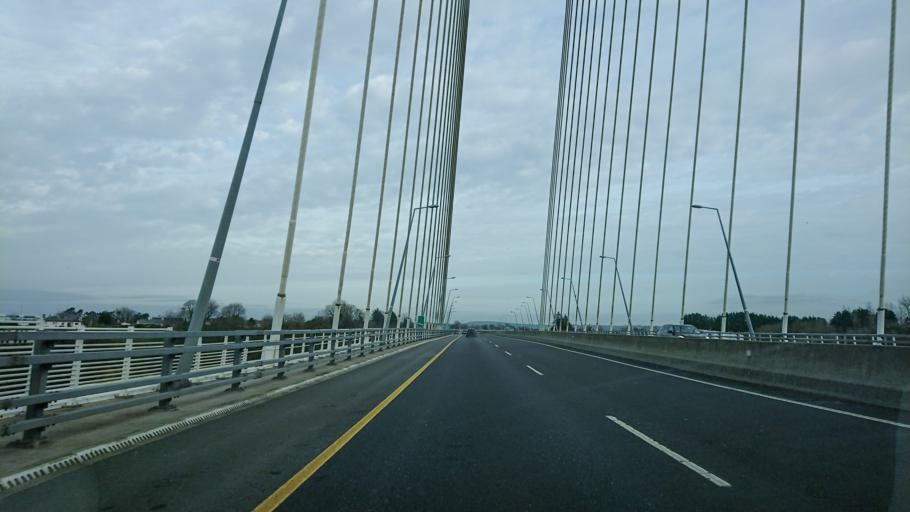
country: IE
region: Munster
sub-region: Waterford
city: Waterford
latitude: 52.2792
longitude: -7.1507
